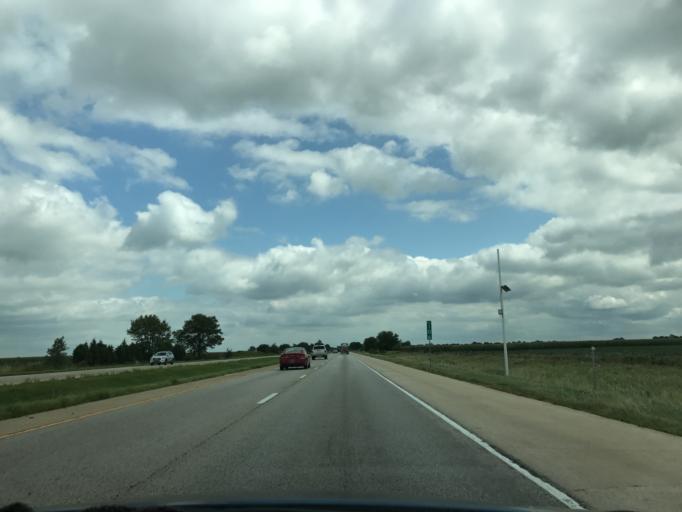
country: US
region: Illinois
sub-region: LaSalle County
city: Seneca
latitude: 41.3773
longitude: -88.5359
